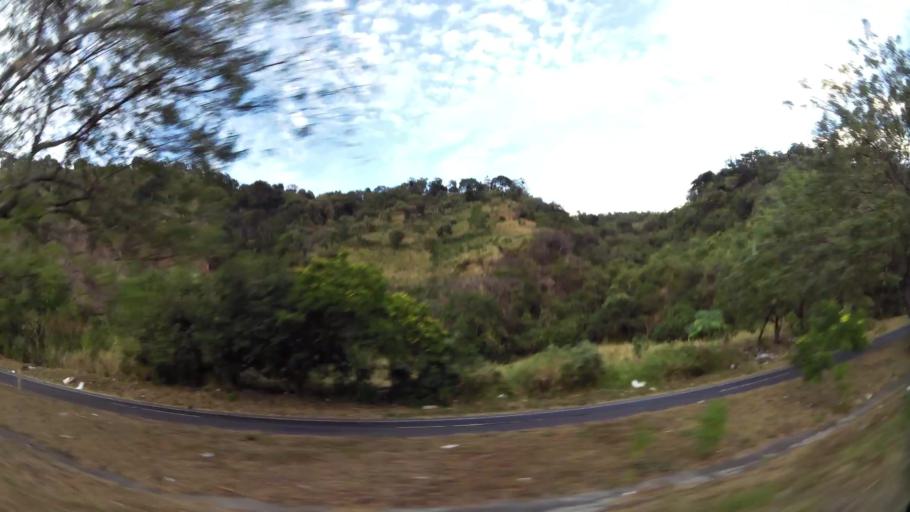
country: SV
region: San Vicente
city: Apastepeque
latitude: 13.6659
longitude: -88.8104
